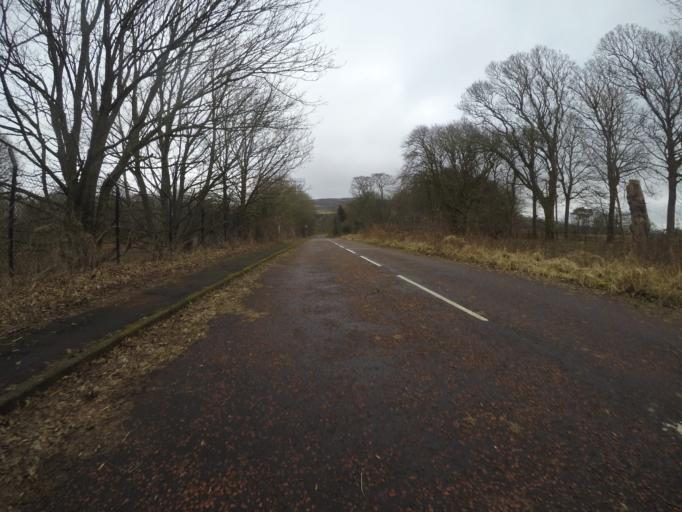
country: GB
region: Scotland
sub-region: North Ayrshire
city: Fairlie
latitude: 55.7294
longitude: -4.8725
